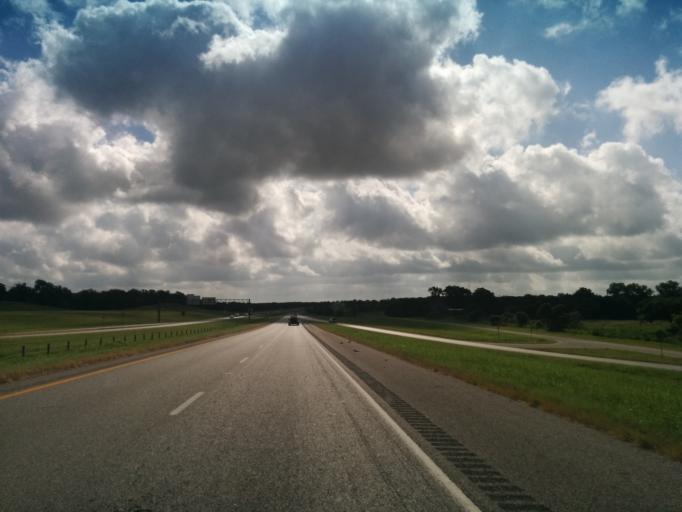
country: US
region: Texas
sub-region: Caldwell County
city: Luling
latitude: 29.6527
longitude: -97.5900
